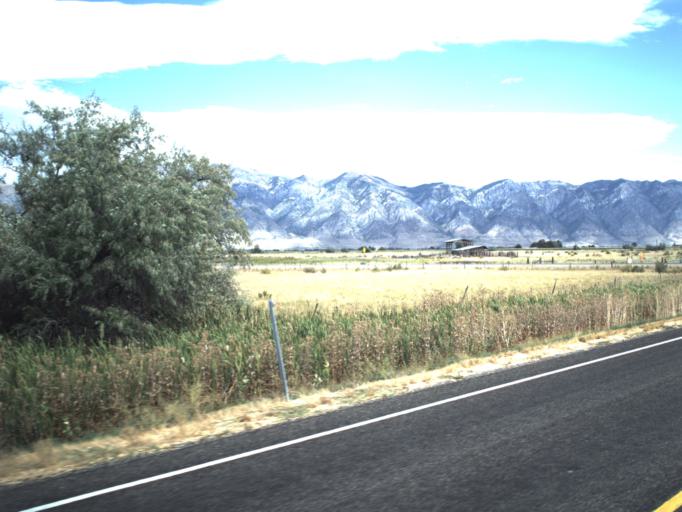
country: US
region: Utah
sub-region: Box Elder County
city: Honeyville
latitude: 41.5656
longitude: -112.1798
